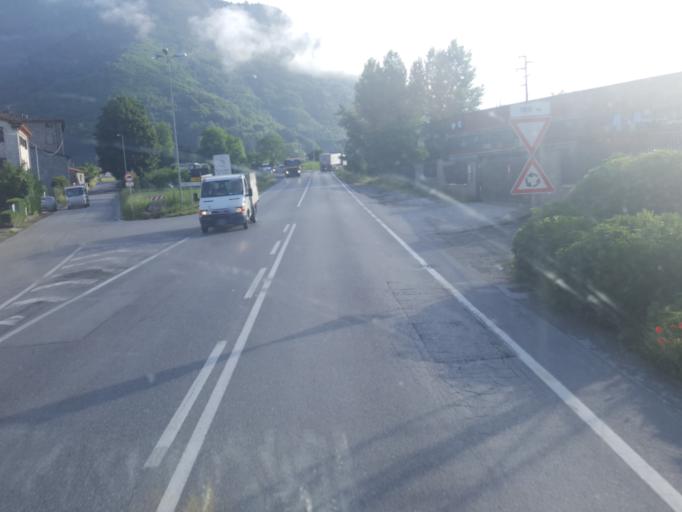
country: IT
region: Tuscany
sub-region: Provincia di Lucca
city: Valdottavo
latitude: 43.9568
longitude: 10.5036
